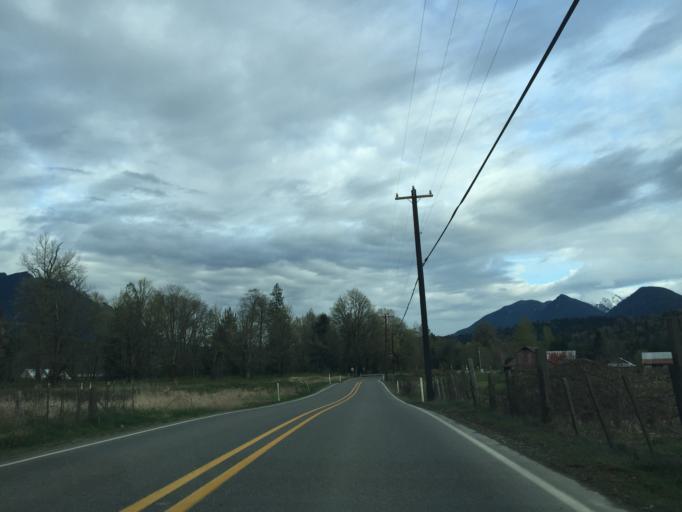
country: US
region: Washington
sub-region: Snohomish County
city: Arlington Heights
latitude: 48.2721
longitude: -121.8933
